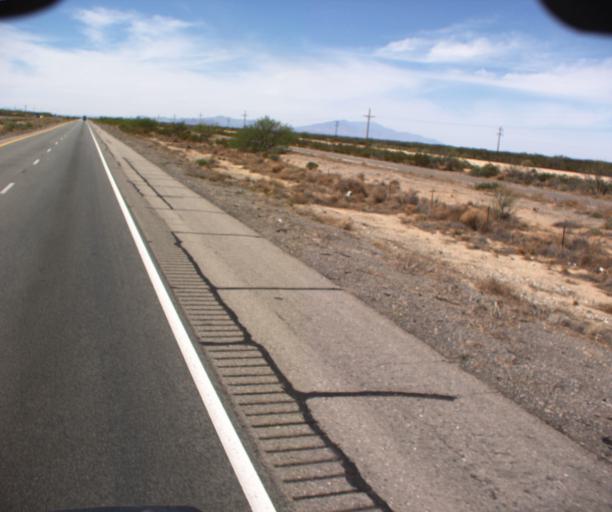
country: US
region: Arizona
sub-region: Cochise County
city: Willcox
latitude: 32.2903
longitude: -109.3227
